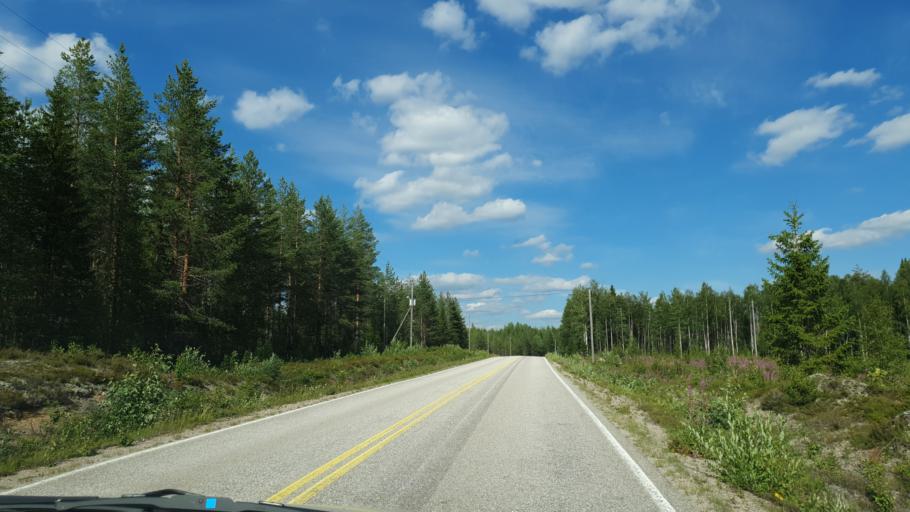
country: FI
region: Kainuu
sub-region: Kajaani
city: Sotkamo
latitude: 64.1981
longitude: 28.9026
